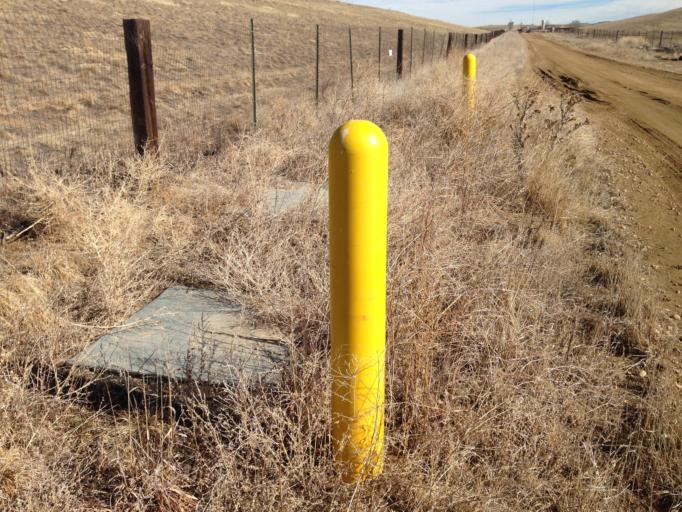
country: US
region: Colorado
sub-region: Boulder County
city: Erie
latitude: 40.0293
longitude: -105.0355
